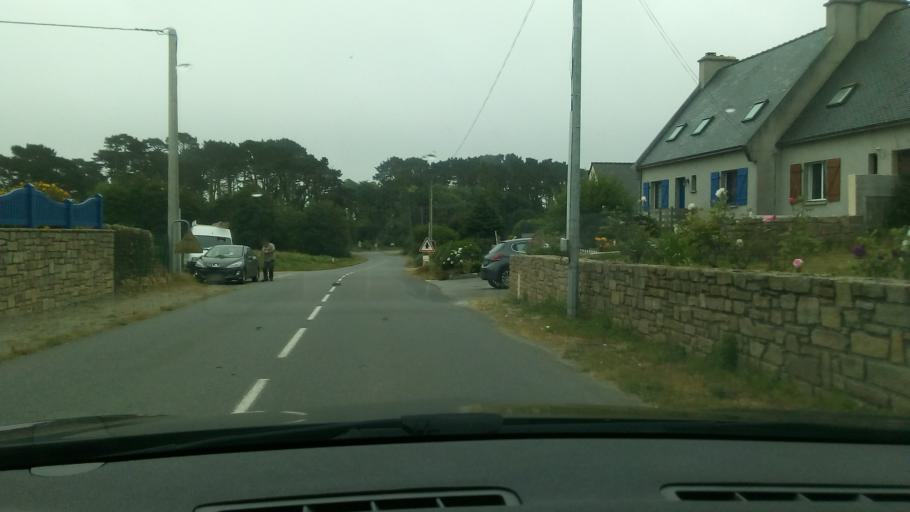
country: FR
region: Brittany
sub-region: Departement du Finistere
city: Le Conquet
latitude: 48.3742
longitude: -4.7475
